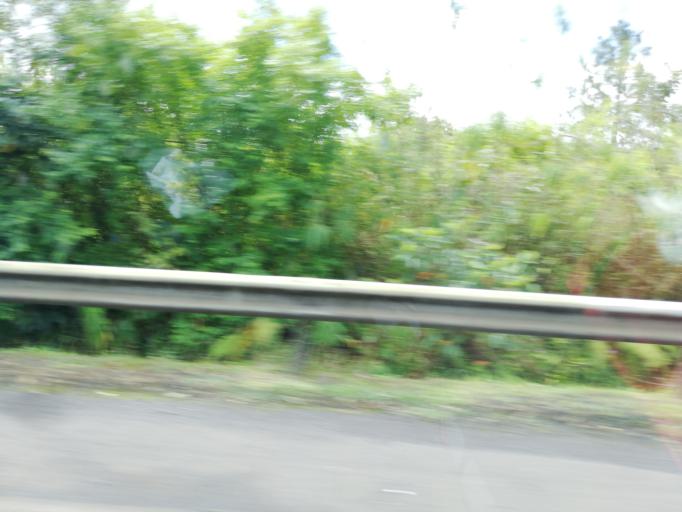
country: MU
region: Plaines Wilhems
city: Midlands
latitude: -20.3497
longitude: 57.5708
